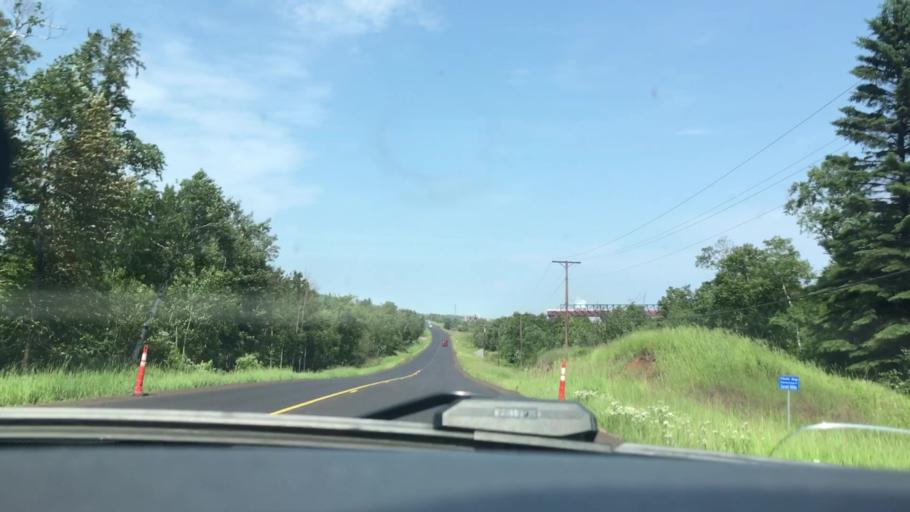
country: US
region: Minnesota
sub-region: Lake County
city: Silver Bay
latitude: 47.2752
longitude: -91.2751
